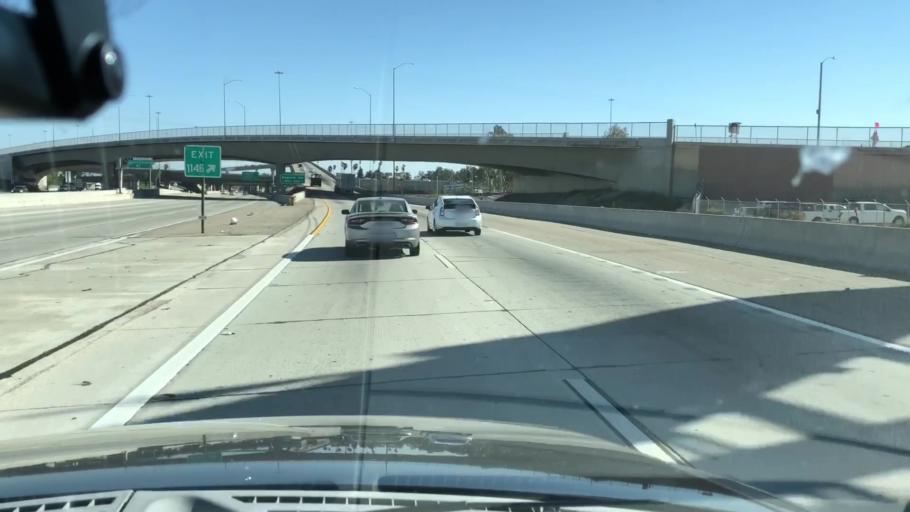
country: US
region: California
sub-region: Orange County
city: Buena Park
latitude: 33.8598
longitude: -117.9882
